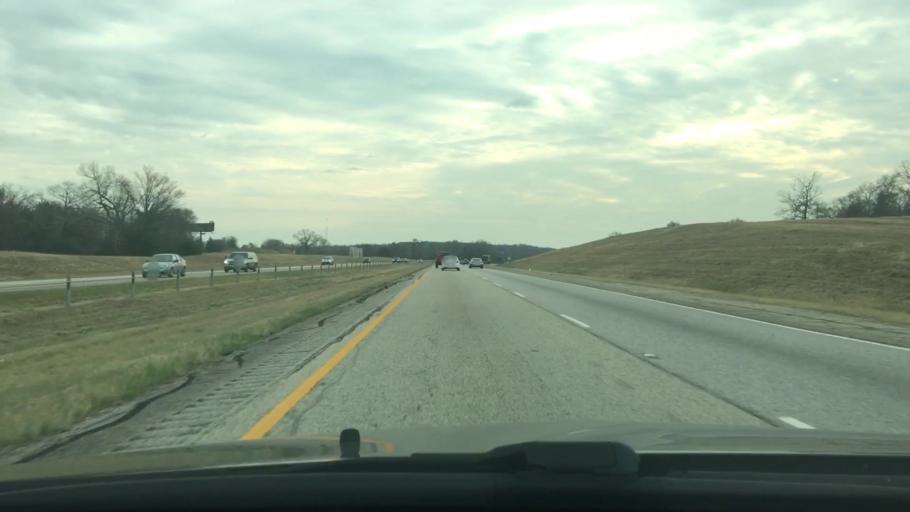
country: US
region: Texas
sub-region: Leon County
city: Centerville
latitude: 31.2518
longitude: -95.9887
